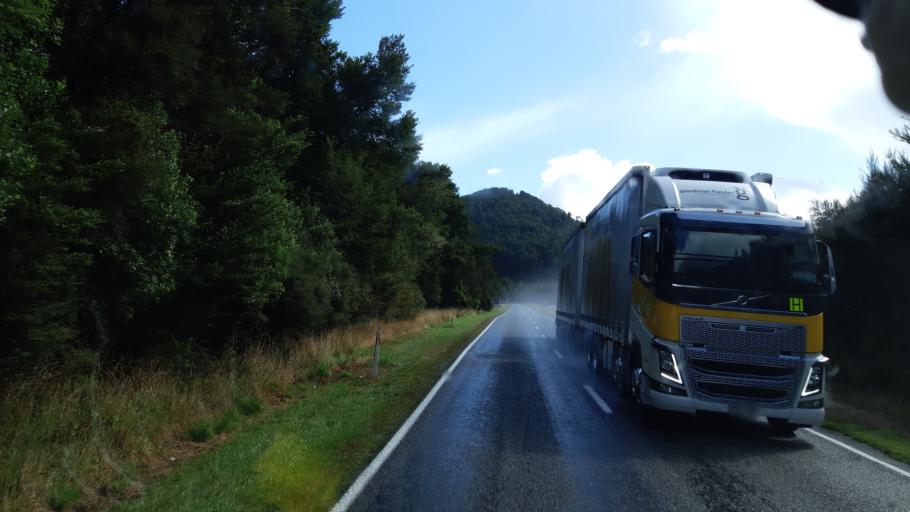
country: NZ
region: West Coast
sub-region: Buller District
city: Westport
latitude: -42.3529
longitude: 172.2302
